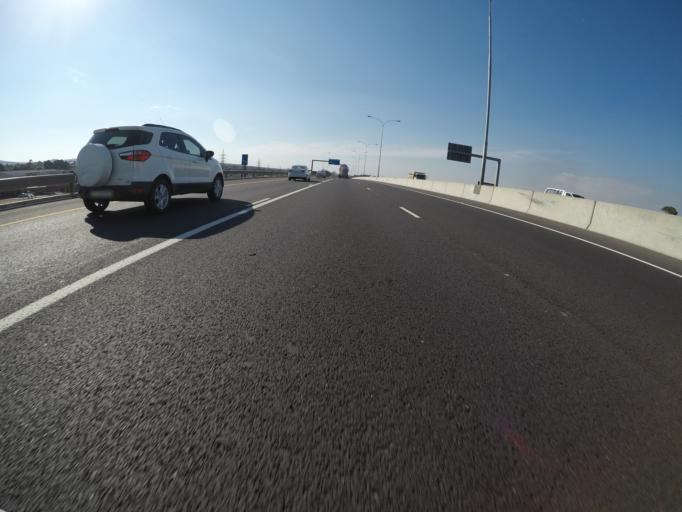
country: ZA
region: Western Cape
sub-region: City of Cape Town
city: Kraaifontein
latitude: -33.8925
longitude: 18.6771
